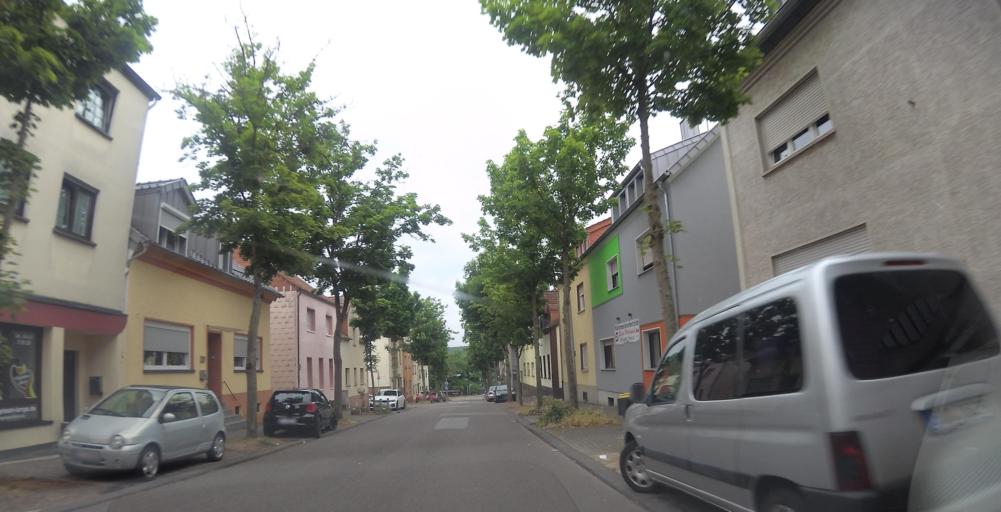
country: DE
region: Saarland
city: Saarbrucken
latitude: 49.2453
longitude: 6.9493
